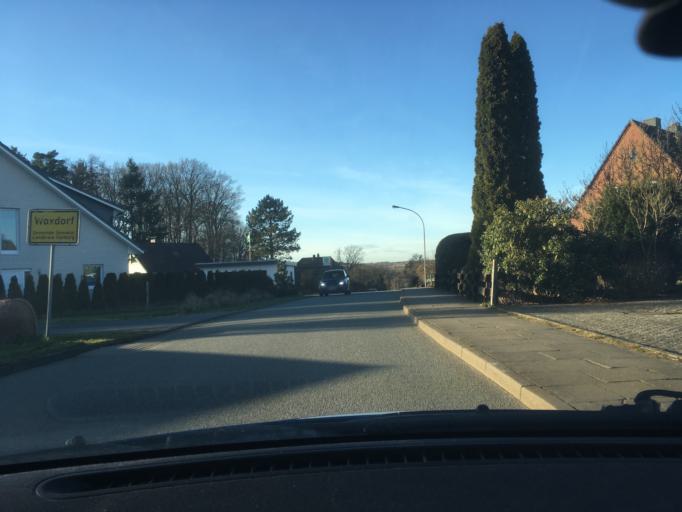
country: DE
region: Lower Saxony
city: Seevetal
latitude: 53.4081
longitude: 9.9629
